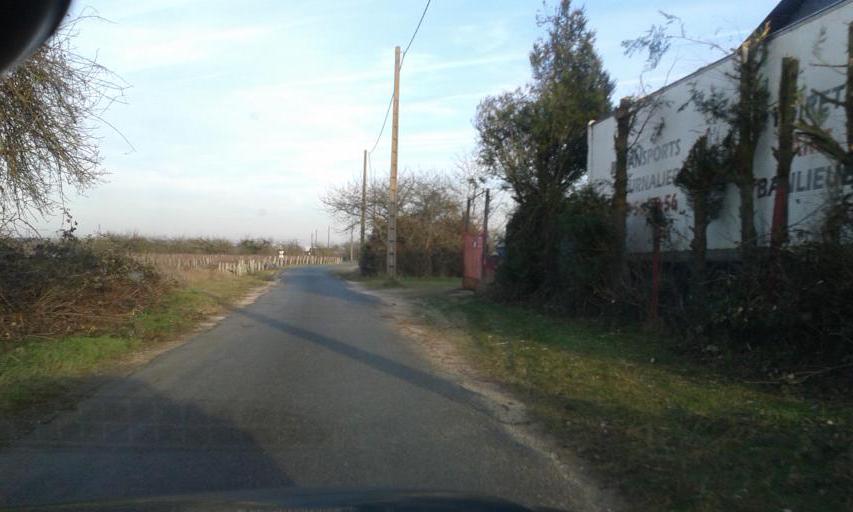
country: FR
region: Centre
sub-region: Departement du Loiret
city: Mareau-aux-Pres
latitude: 47.8539
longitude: 1.8052
